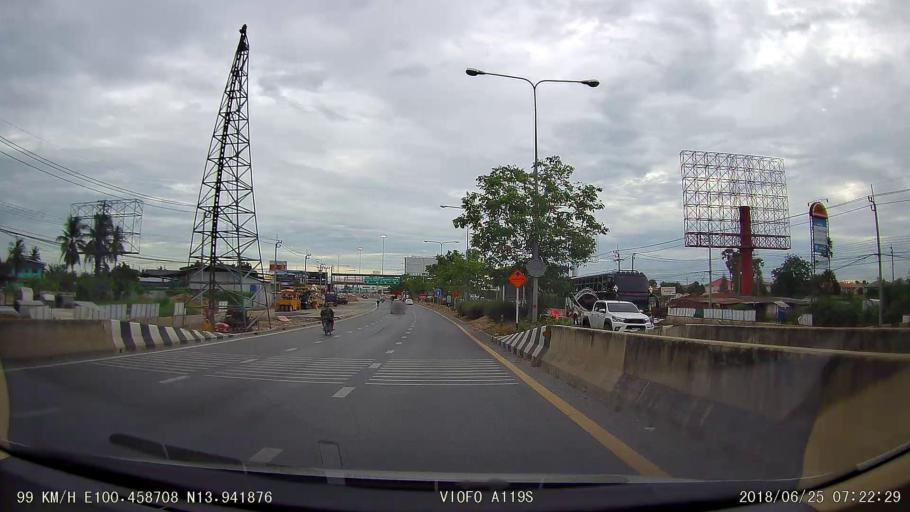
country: TH
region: Nonthaburi
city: Bang Bua Thong
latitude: 13.9422
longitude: 100.4589
